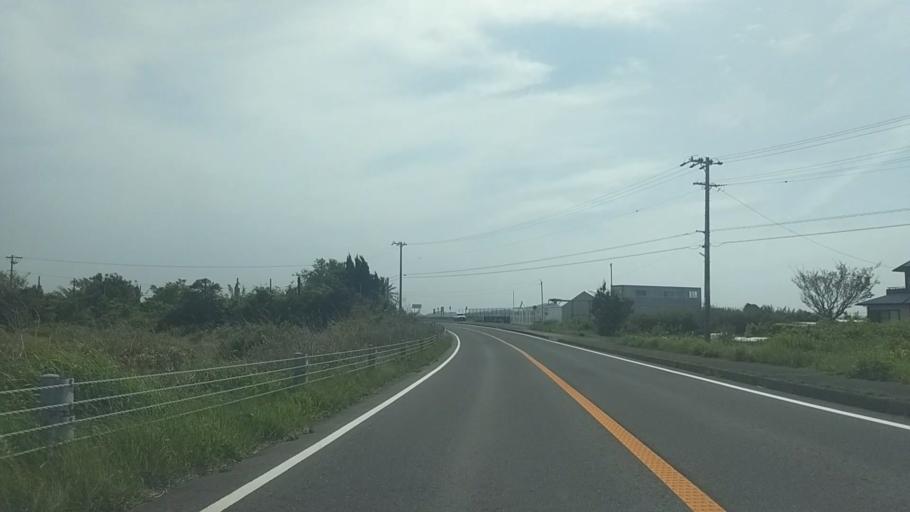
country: JP
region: Shizuoka
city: Kosai-shi
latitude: 34.7228
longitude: 137.5882
